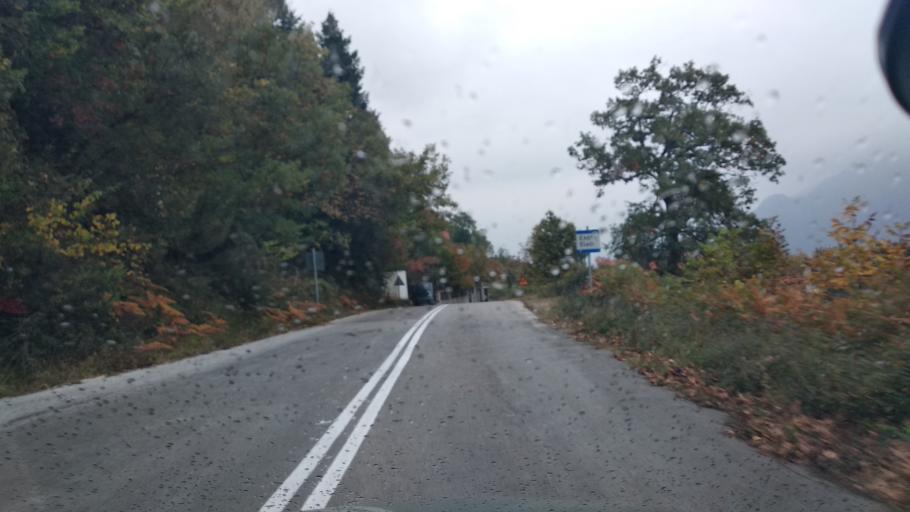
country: GR
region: Thessaly
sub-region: Trikala
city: Pyli
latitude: 39.5093
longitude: 21.5338
